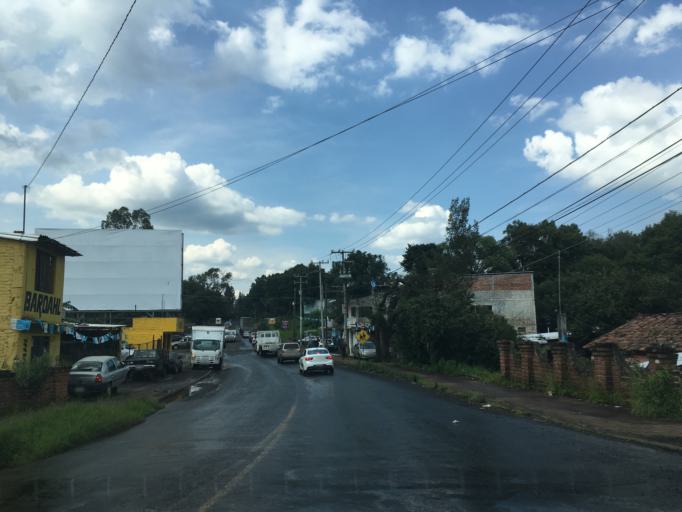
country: MX
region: Michoacan
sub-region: Tingueindin
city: Tingueindin
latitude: 19.7425
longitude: -102.4841
